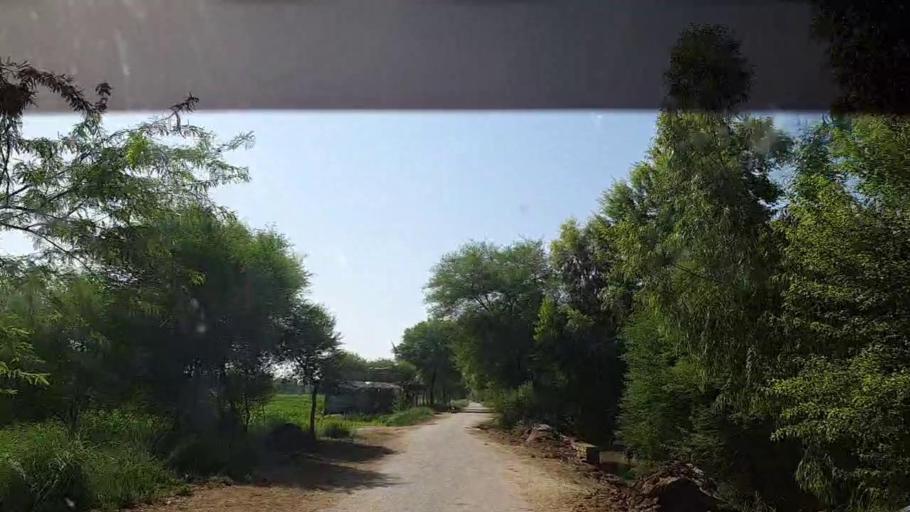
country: PK
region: Sindh
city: Ghauspur
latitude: 28.1734
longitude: 69.0545
